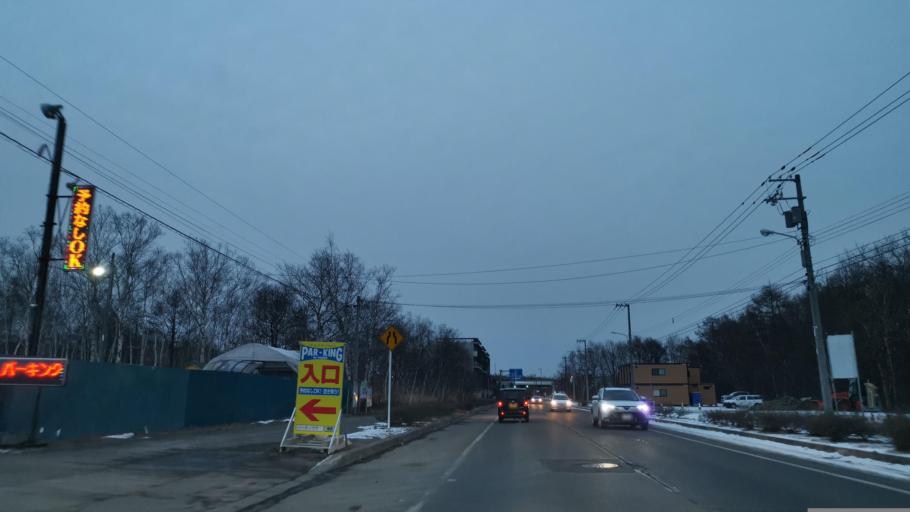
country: JP
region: Hokkaido
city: Chitose
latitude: 42.8153
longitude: 141.6748
